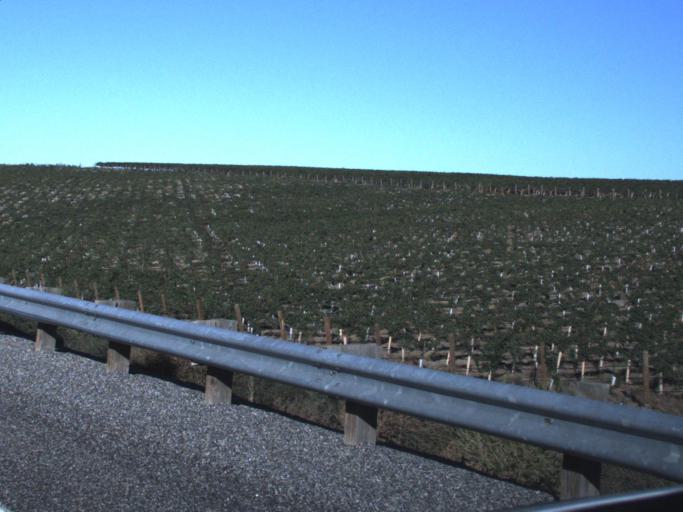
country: US
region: Washington
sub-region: Benton County
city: Benton City
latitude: 46.2622
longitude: -119.4600
